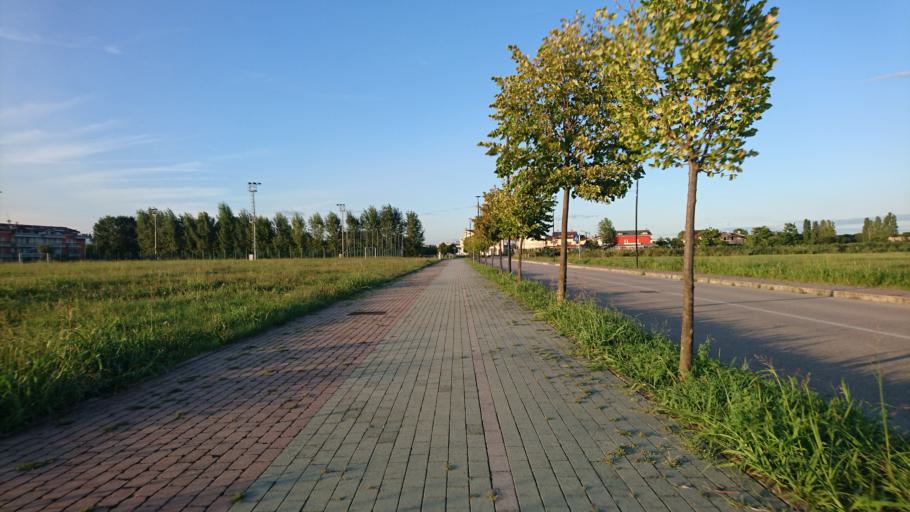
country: IT
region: Veneto
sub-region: Provincia di Padova
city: Montegrotto Terme
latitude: 45.3406
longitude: 11.7890
